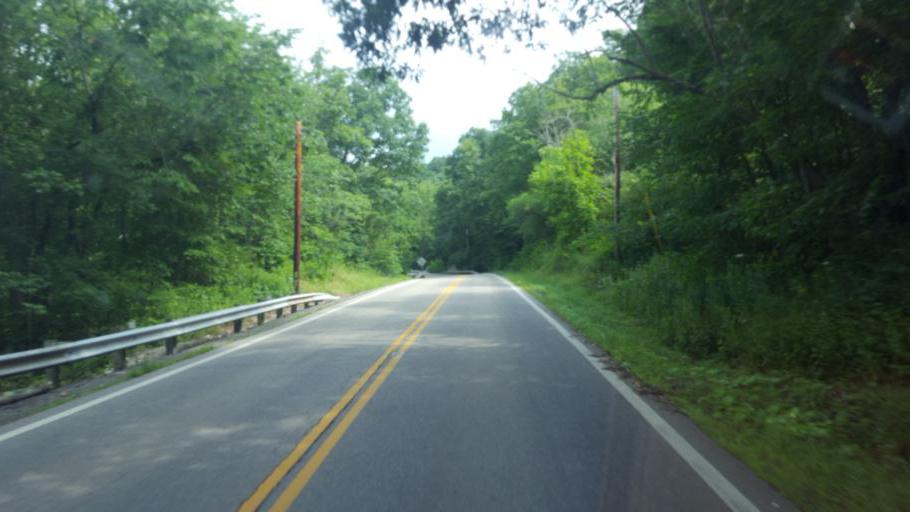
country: US
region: Ohio
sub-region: Columbiana County
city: Salineville
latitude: 40.6436
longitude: -80.8060
